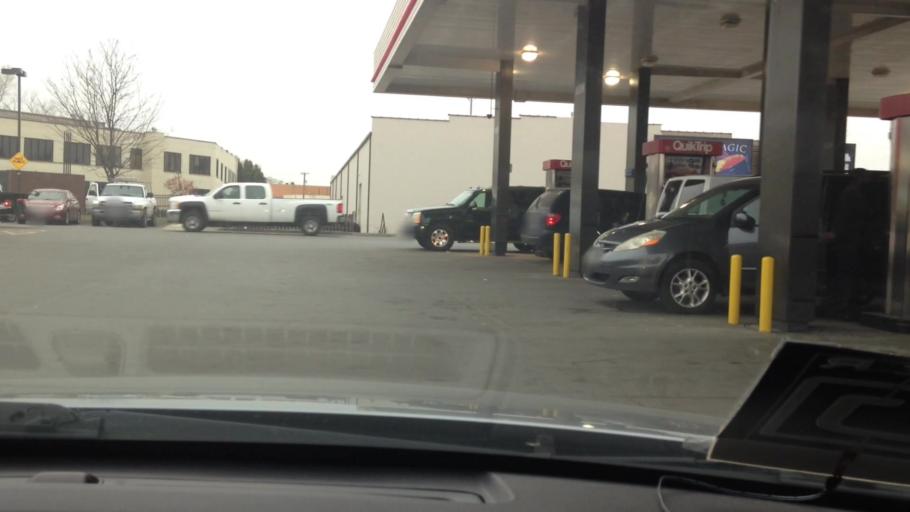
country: US
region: Kansas
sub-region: Johnson County
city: Westwood
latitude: 39.0719
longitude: -94.6071
